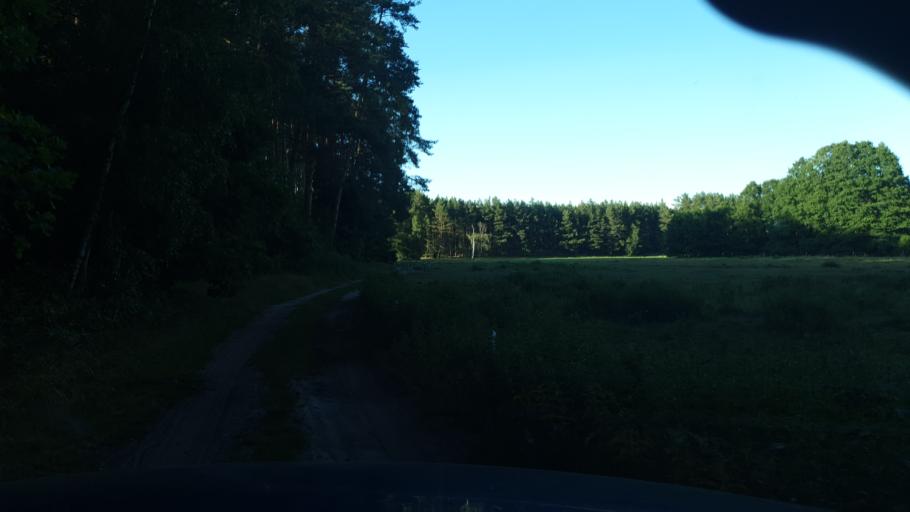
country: PL
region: Pomeranian Voivodeship
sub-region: Powiat bytowski
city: Lipnica
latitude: 53.8881
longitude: 17.4254
